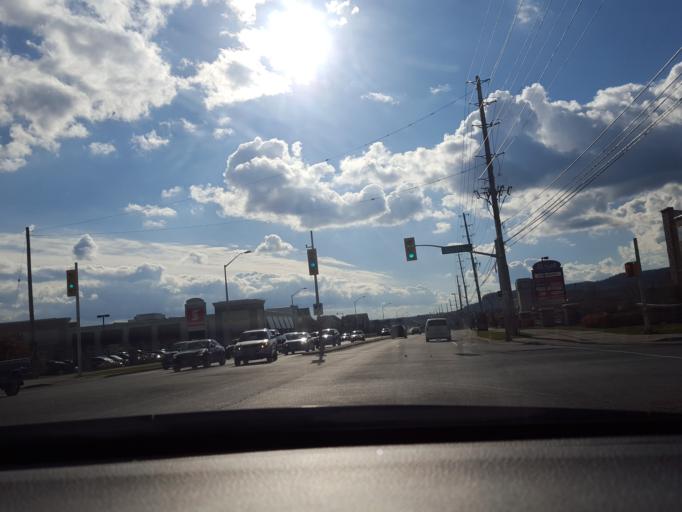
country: CA
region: Ontario
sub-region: Halton
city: Milton
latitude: 43.4922
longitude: -79.8771
